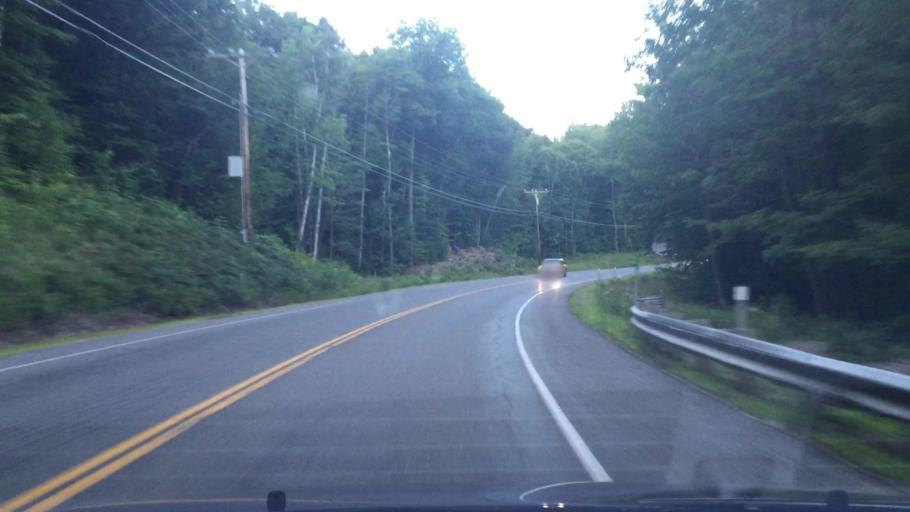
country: US
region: New Hampshire
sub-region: Grafton County
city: Woodstock
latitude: 44.0614
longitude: -71.6222
